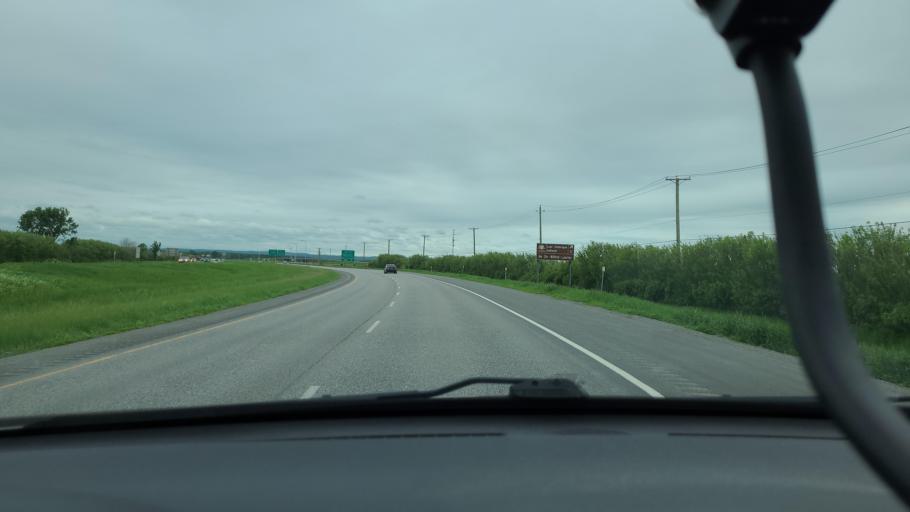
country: CA
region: Quebec
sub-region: Lanaudiere
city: Sainte-Julienne
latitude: 45.8774
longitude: -73.6501
